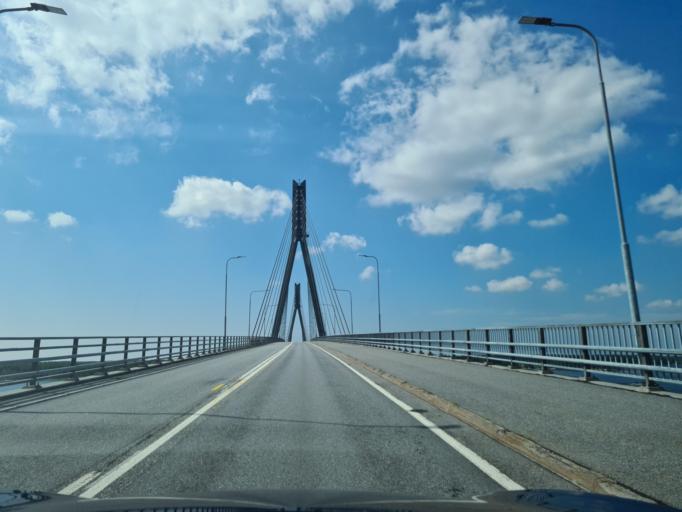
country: FI
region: Ostrobothnia
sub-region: Vaasa
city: Replot
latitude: 63.2068
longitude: 21.4792
